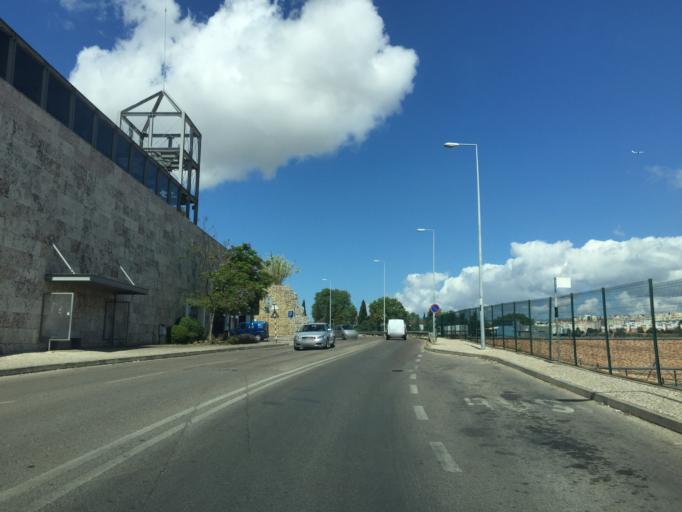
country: PT
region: Setubal
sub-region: Almada
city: Pragal
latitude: 38.6585
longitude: -9.1737
